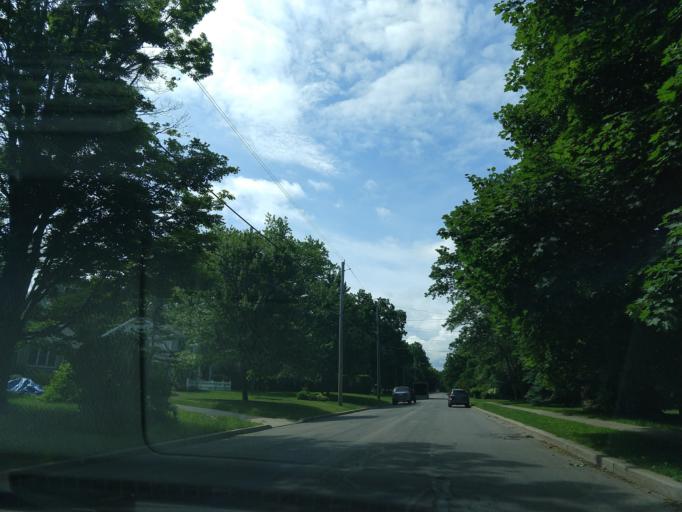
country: US
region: New York
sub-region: Erie County
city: East Aurora
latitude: 42.7623
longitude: -78.6041
